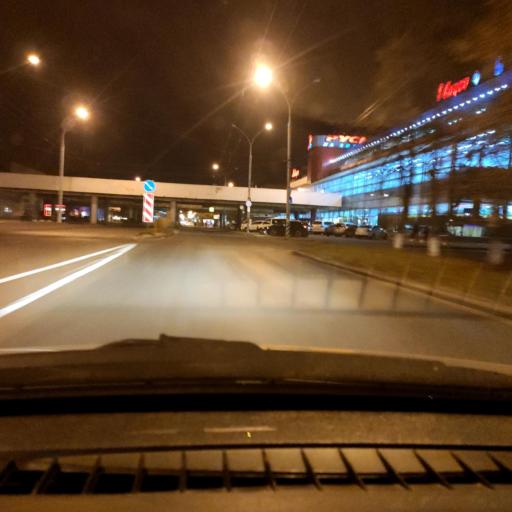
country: RU
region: Samara
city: Tol'yatti
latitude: 53.5190
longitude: 49.2737
